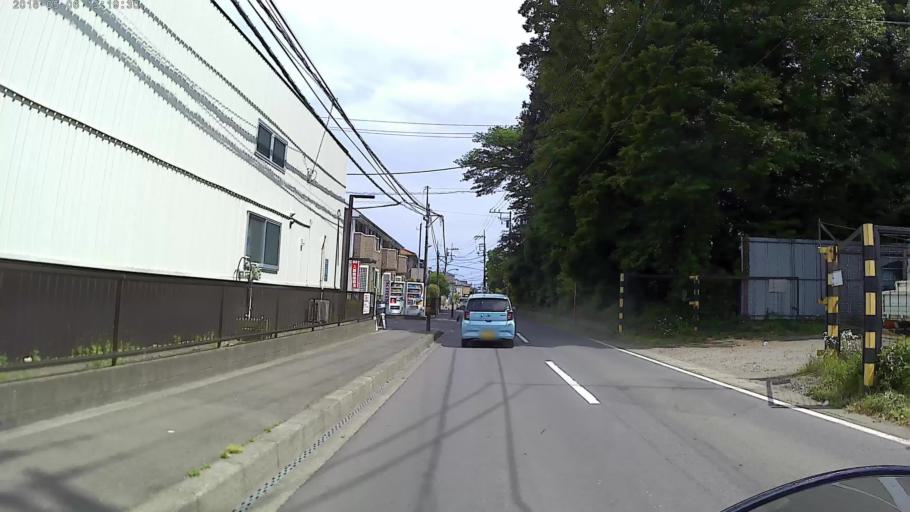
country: JP
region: Kanagawa
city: Minami-rinkan
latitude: 35.4141
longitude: 139.4408
